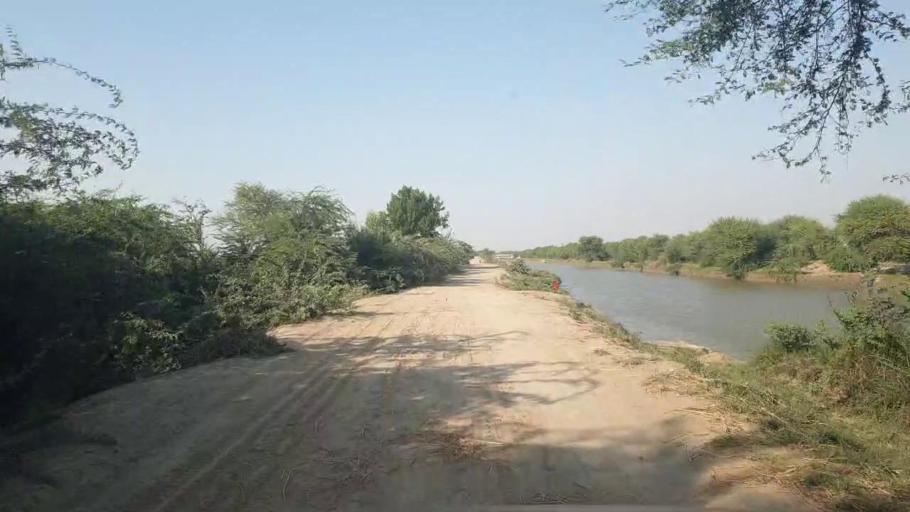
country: PK
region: Sindh
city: Badin
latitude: 24.6339
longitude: 68.8150
